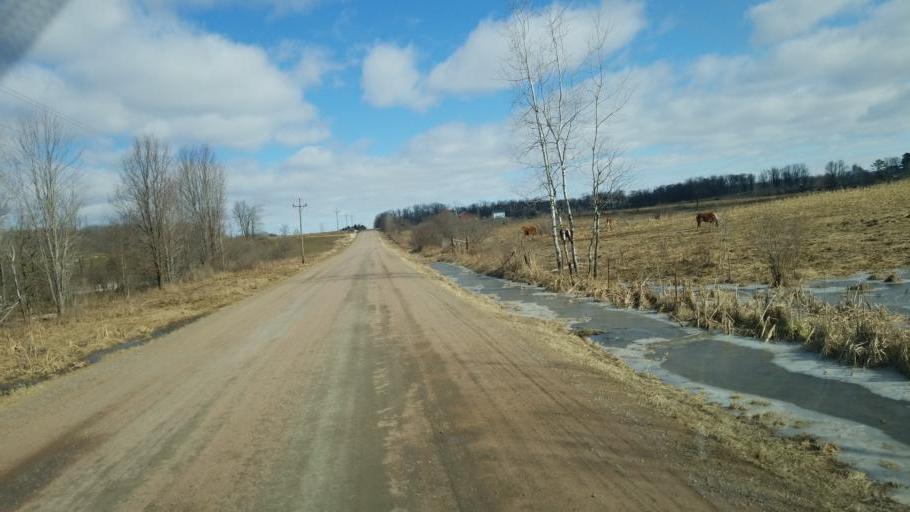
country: US
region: Wisconsin
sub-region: Clark County
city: Loyal
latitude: 44.6332
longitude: -90.4358
